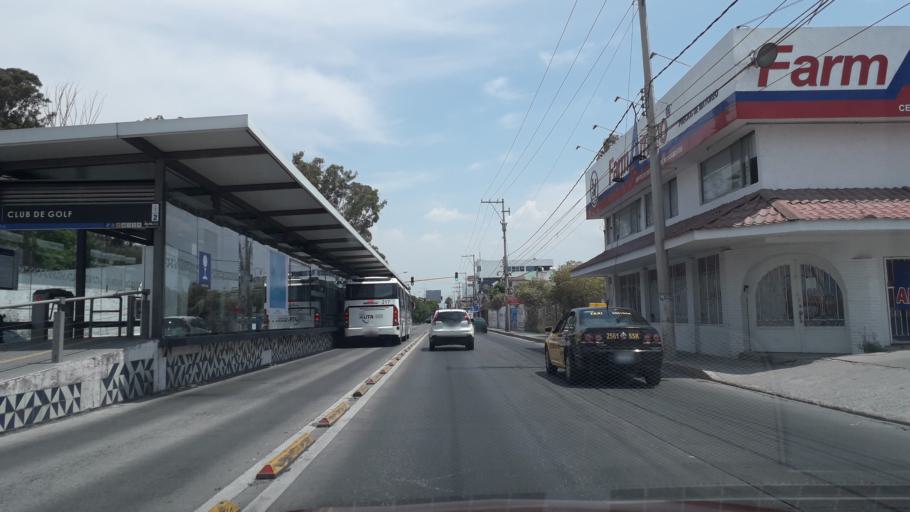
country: MX
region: Puebla
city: Puebla
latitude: 19.0126
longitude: -98.2335
